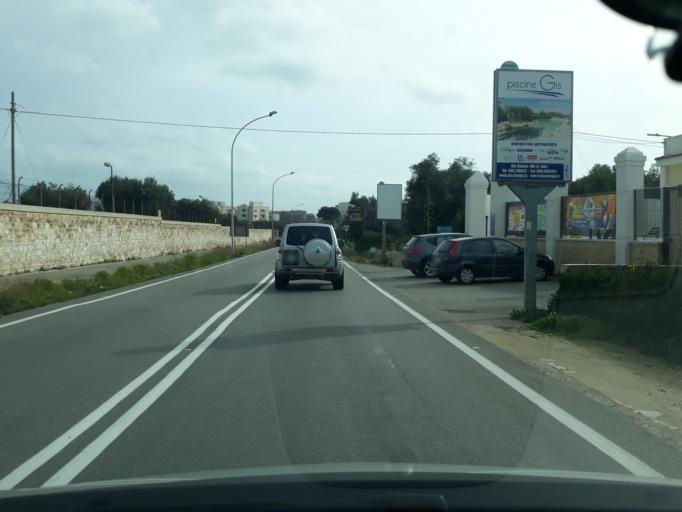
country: IT
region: Apulia
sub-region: Provincia di Bari
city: Monopoli
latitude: 40.9540
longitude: 17.2838
